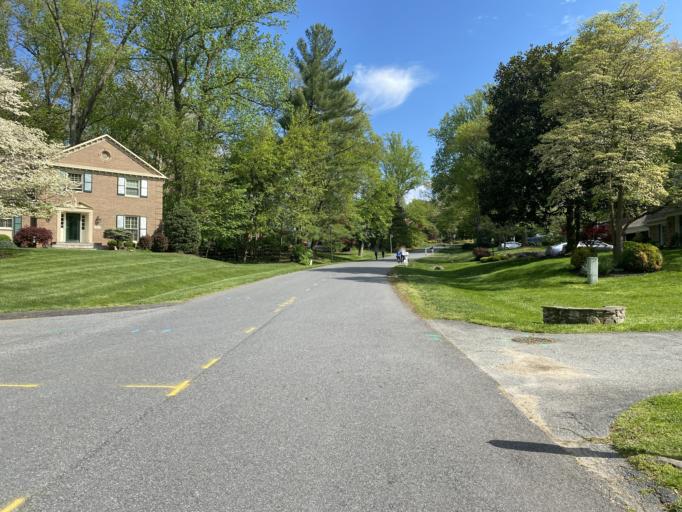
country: US
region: Maryland
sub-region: Montgomery County
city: Potomac
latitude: 39.0518
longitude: -77.2046
